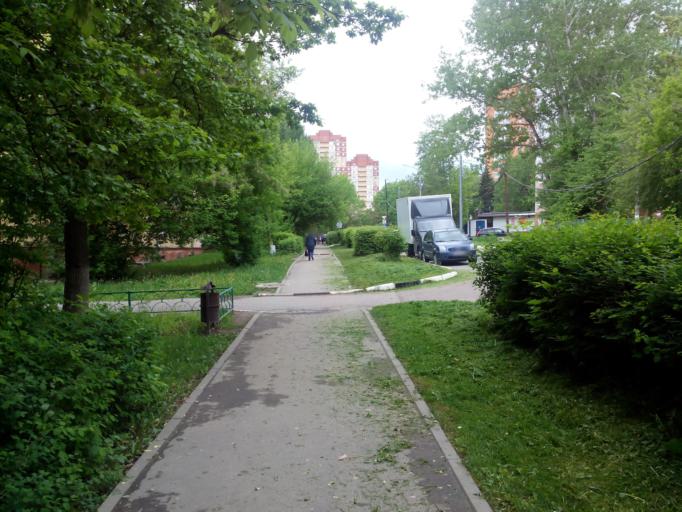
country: RU
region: Moskovskaya
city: Odintsovo
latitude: 55.6655
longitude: 37.2892
